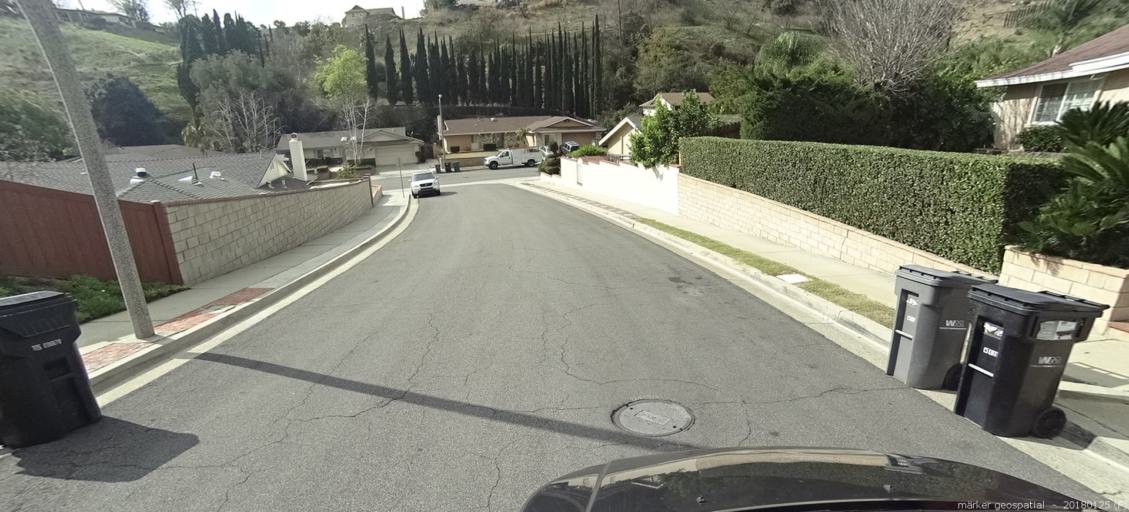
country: US
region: California
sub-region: Los Angeles County
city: Diamond Bar
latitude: 33.9870
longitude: -117.8320
